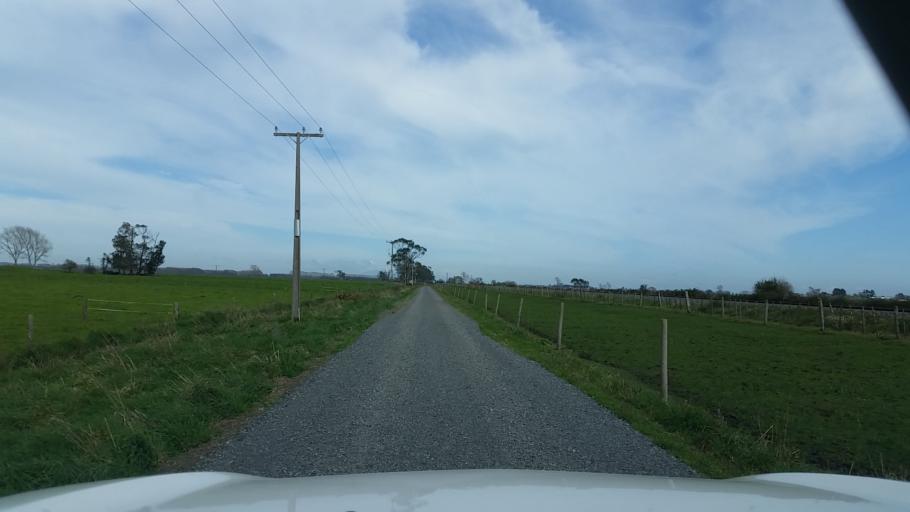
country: NZ
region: Waikato
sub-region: Waipa District
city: Cambridge
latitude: -37.6826
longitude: 175.4551
